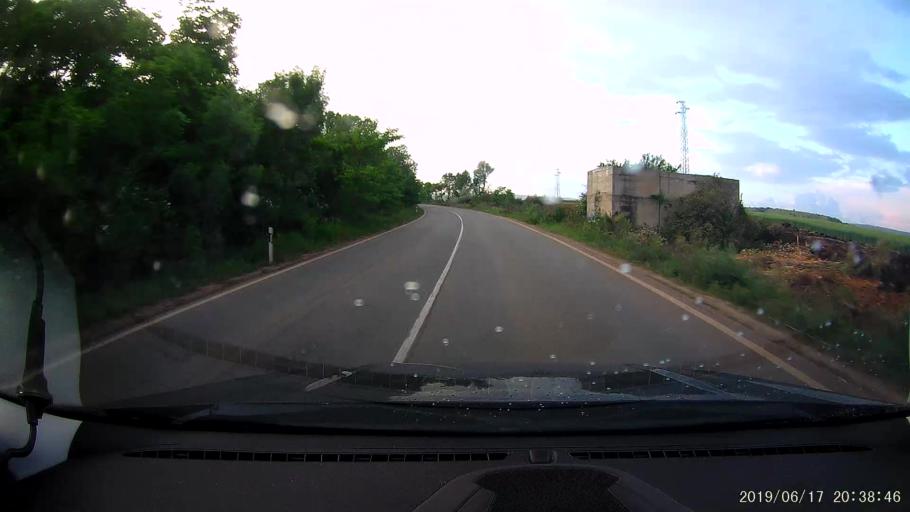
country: BG
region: Sofiya
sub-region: Obshtina Slivnitsa
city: Slivnitsa
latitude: 42.8771
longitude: 23.0185
